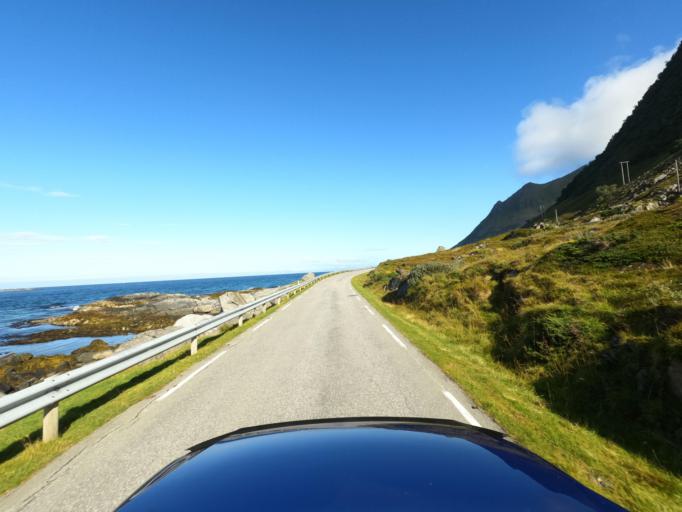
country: NO
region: Nordland
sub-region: Vagan
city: Kabelvag
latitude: 68.3192
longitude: 14.3094
